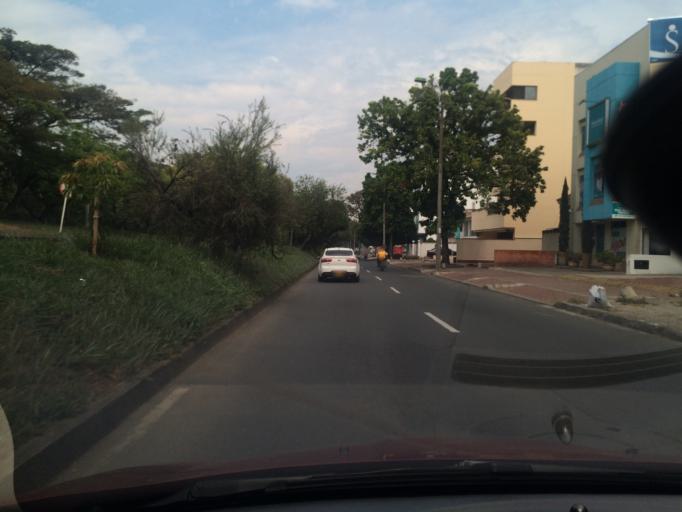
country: CO
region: Valle del Cauca
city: Cali
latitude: 3.3695
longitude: -76.5343
